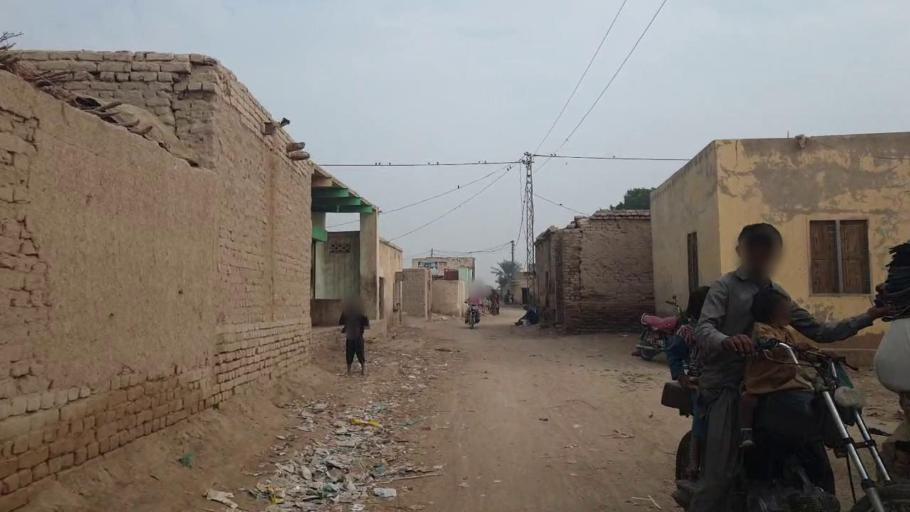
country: PK
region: Sindh
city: Sann
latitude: 25.9767
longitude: 68.1910
